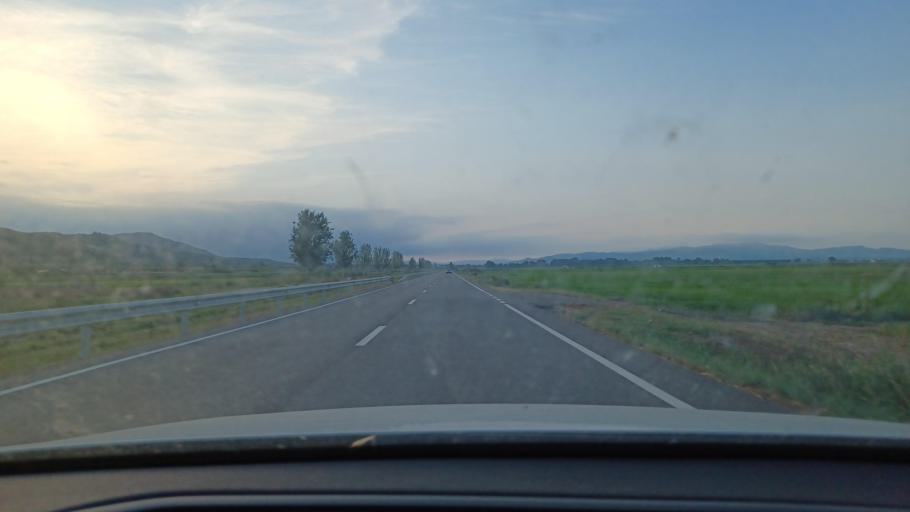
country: ES
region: Catalonia
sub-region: Provincia de Tarragona
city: Sant Carles de la Rapita
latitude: 40.6510
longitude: 0.5965
